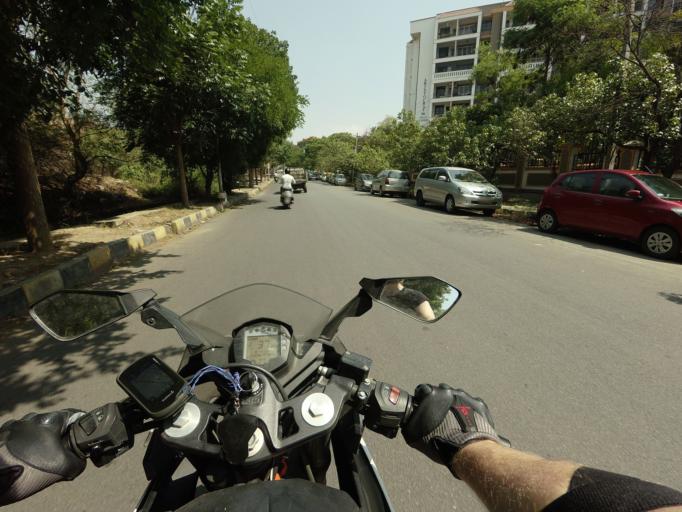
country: IN
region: Karnataka
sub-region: Bangalore Urban
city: Bangalore
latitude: 13.0009
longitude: 77.6607
